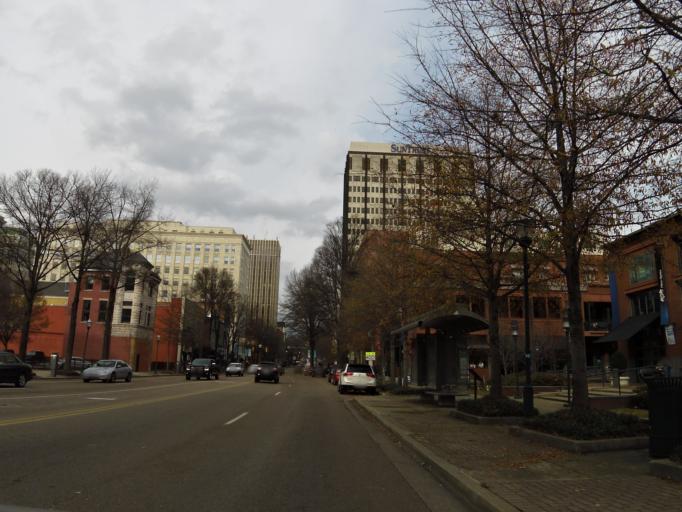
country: US
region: Tennessee
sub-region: Hamilton County
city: Chattanooga
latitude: 35.0459
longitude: -85.3093
